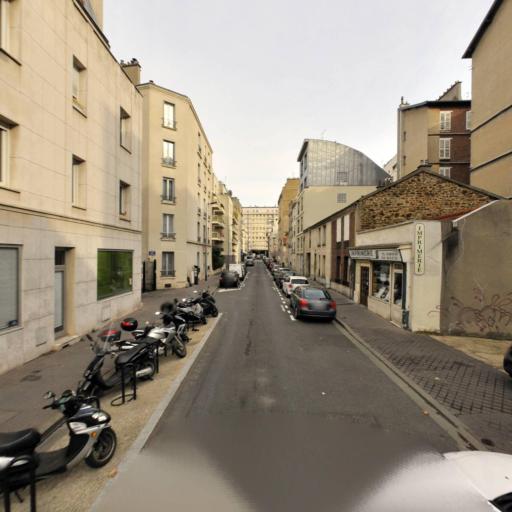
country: FR
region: Ile-de-France
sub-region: Departement des Hauts-de-Seine
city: Boulogne-Billancourt
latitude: 48.8364
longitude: 2.2510
